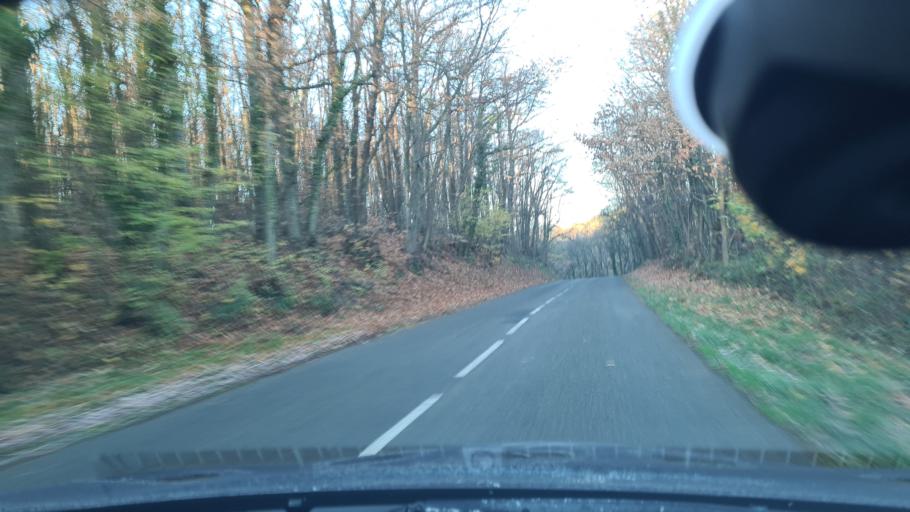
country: FR
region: Rhone-Alpes
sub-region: Departement du Rhone
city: Limonest
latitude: 45.8422
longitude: 4.7870
